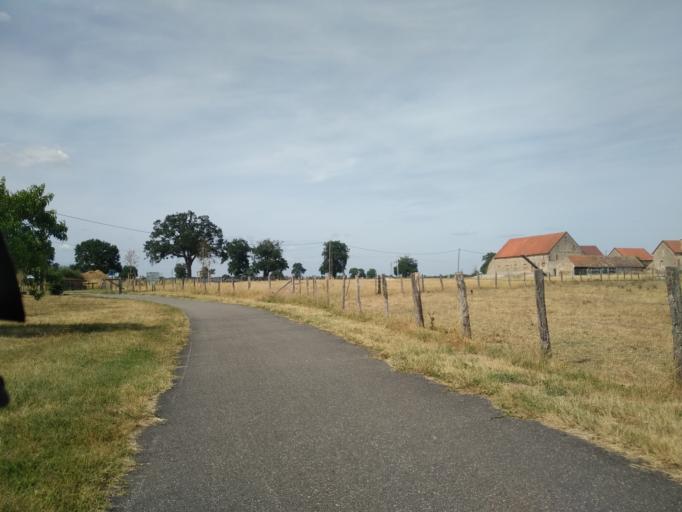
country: FR
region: Bourgogne
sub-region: Departement de Saone-et-Loire
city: Bourbon-Lancy
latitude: 46.6116
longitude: 3.7434
